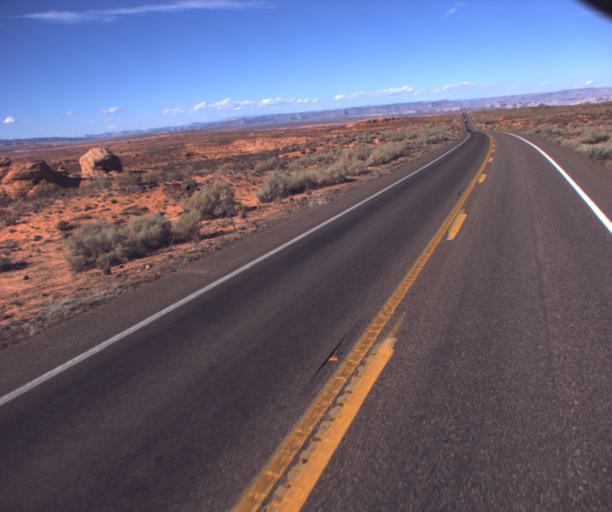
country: US
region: Arizona
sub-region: Coconino County
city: LeChee
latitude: 36.8337
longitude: -111.5086
